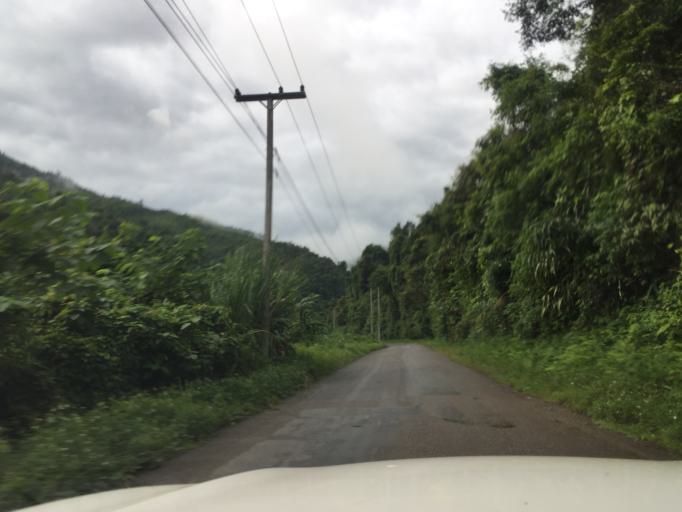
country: LA
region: Oudomxai
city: Muang La
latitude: 21.0611
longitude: 102.2407
